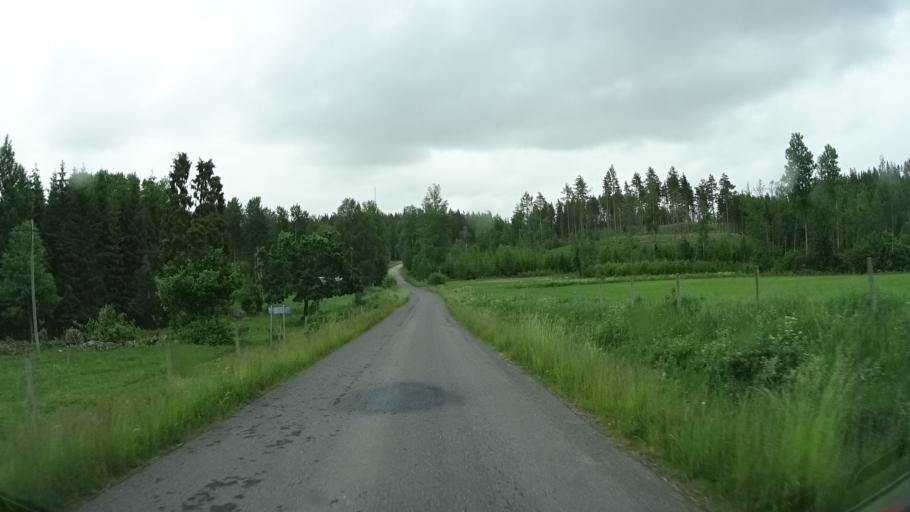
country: SE
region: Joenkoeping
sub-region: Eksjo Kommun
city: Mariannelund
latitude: 57.6903
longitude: 15.5597
